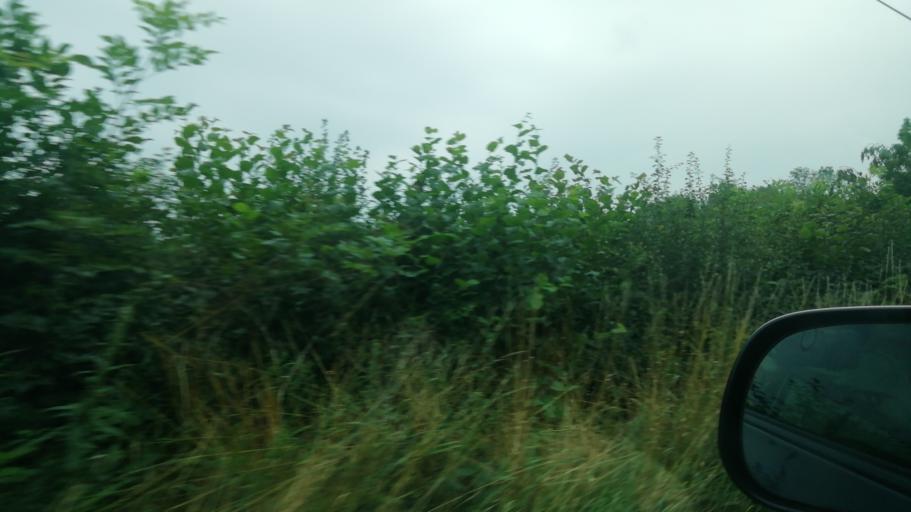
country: IE
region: Munster
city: Fethard
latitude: 52.5283
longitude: -7.6807
